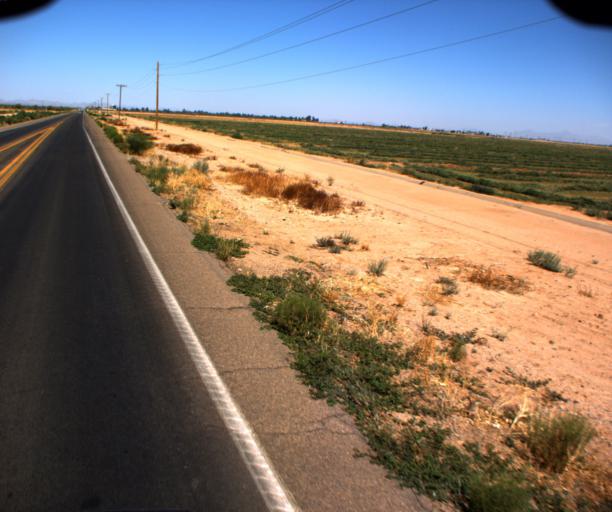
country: US
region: Arizona
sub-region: Pinal County
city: Casa Grande
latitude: 32.8794
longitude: -111.8099
